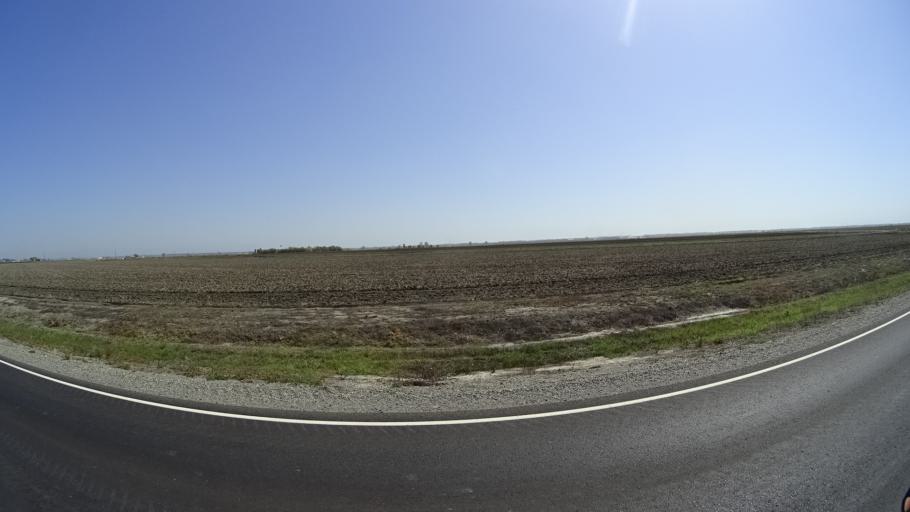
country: US
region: California
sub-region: Glenn County
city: Willows
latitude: 39.5475
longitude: -122.0652
